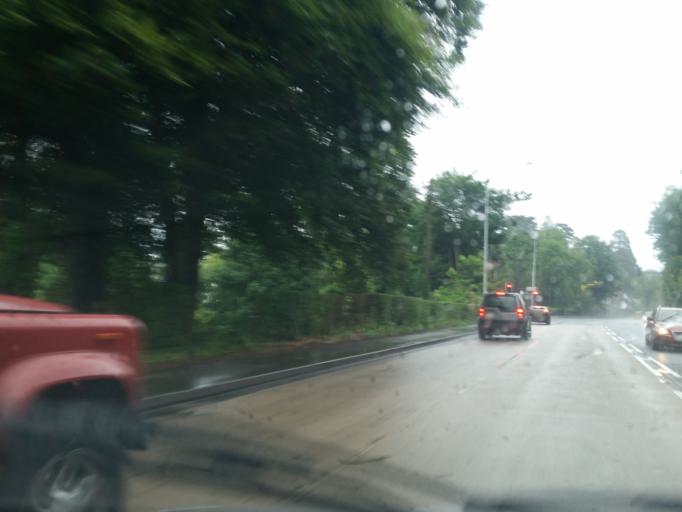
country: GB
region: Northern Ireland
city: Holywood
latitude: 54.6499
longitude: -5.8061
